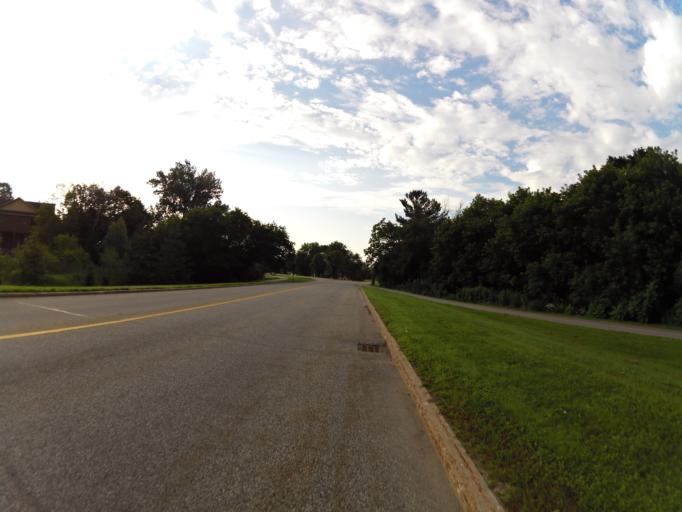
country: CA
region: Ontario
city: Ottawa
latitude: 45.4268
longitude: -75.7381
